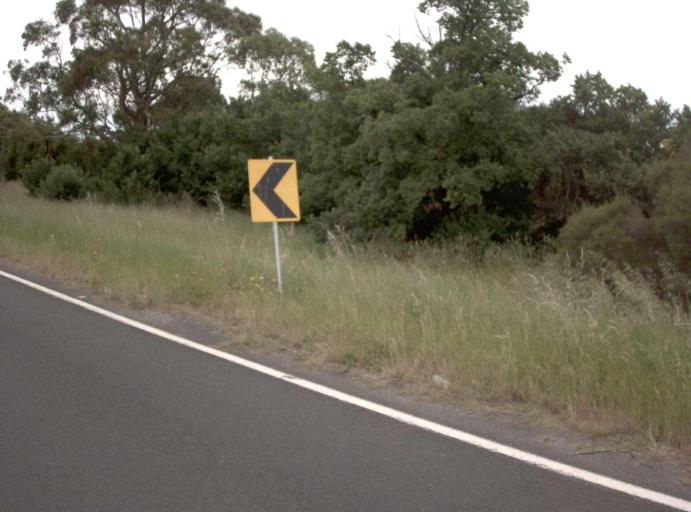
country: AU
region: Victoria
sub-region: Cardinia
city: Koo-Wee-Rup
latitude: -38.2796
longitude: 145.5465
